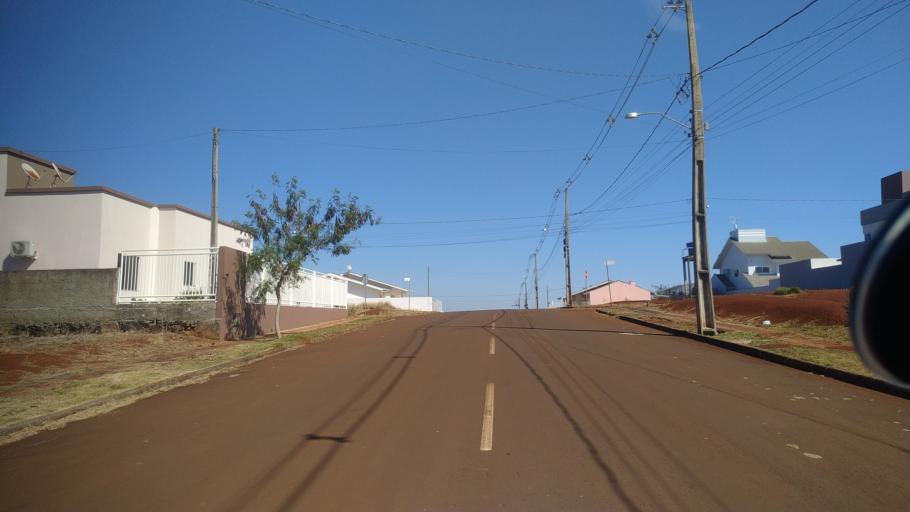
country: BR
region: Santa Catarina
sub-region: Chapeco
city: Chapeco
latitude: -27.0898
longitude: -52.5801
